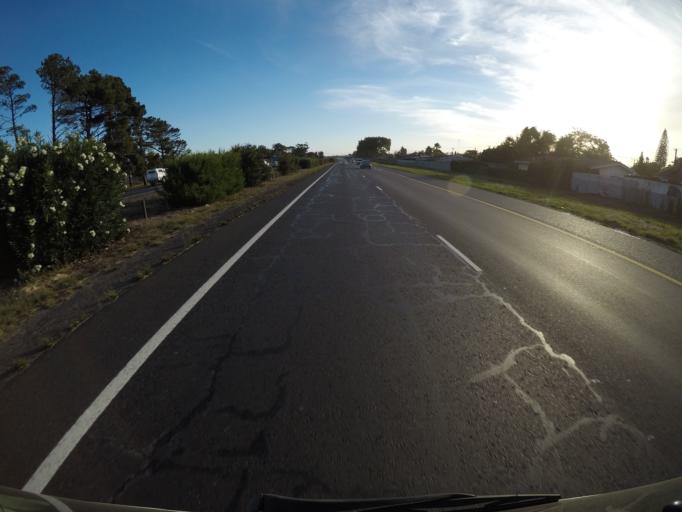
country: ZA
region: Western Cape
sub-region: City of Cape Town
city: Kraaifontein
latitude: -33.8423
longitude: 18.7195
